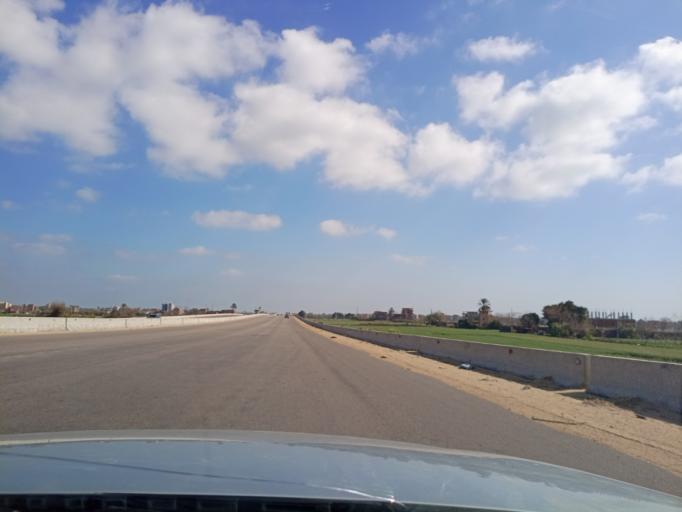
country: EG
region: Muhafazat al Minufiyah
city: Al Bajur
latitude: 30.3981
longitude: 31.0173
